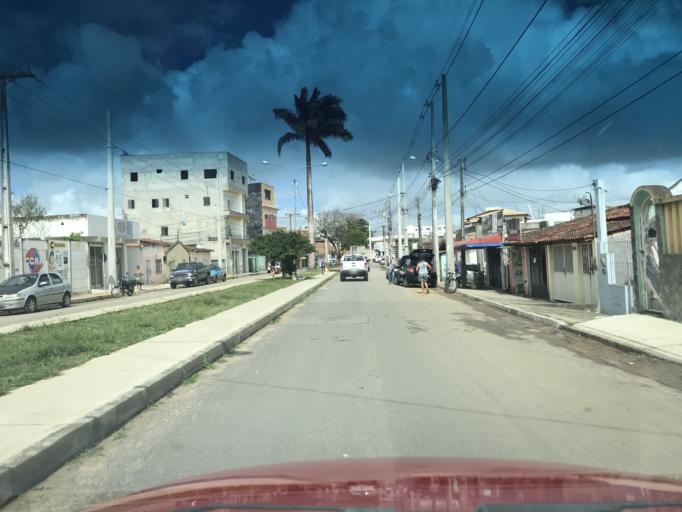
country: BR
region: Bahia
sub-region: Santo Antonio De Jesus
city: Santo Antonio de Jesus
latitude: -12.9778
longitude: -39.2755
